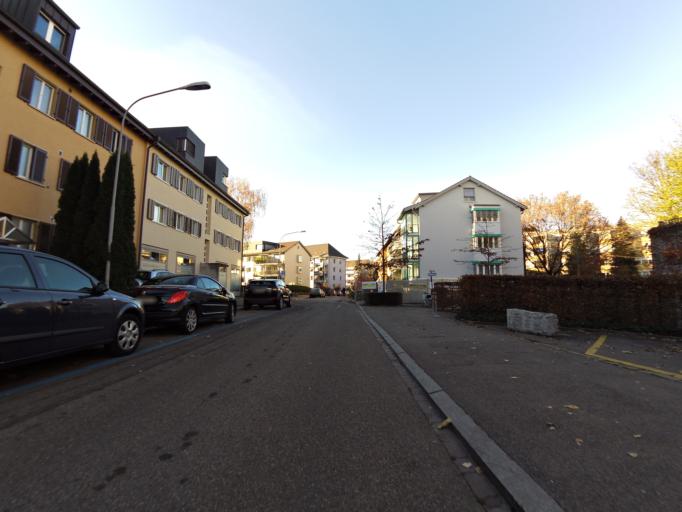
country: CH
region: Zurich
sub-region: Bezirk Zuerich
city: Zuerich (Kreis 3) / Sihlfeld
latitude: 47.3688
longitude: 8.5092
